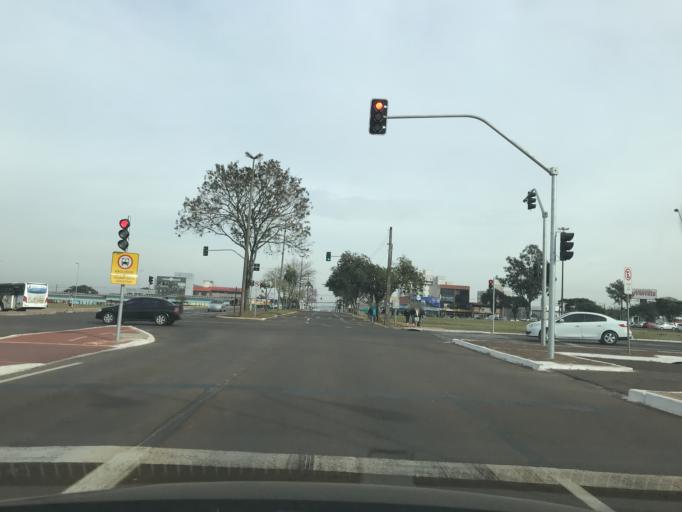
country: BR
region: Parana
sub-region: Cascavel
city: Cascavel
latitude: -24.9543
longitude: -53.4780
